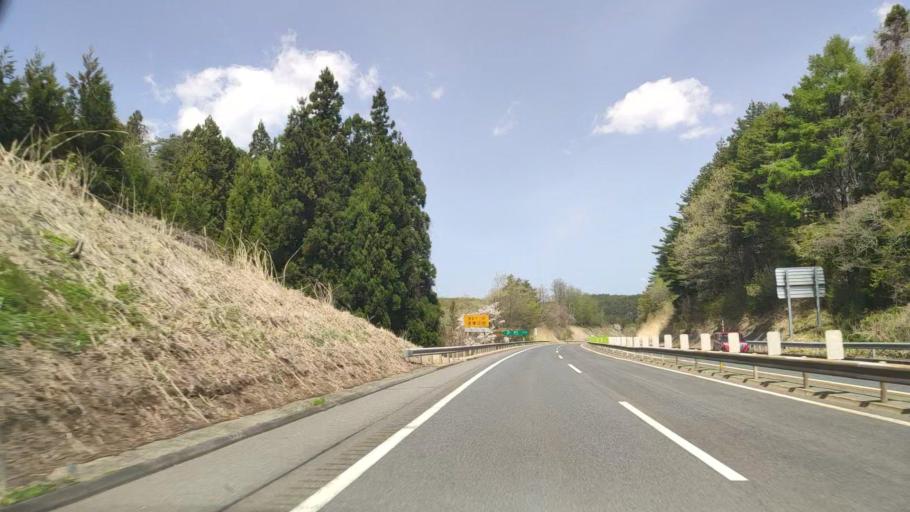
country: JP
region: Aomori
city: Hachinohe
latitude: 40.4176
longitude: 141.4407
